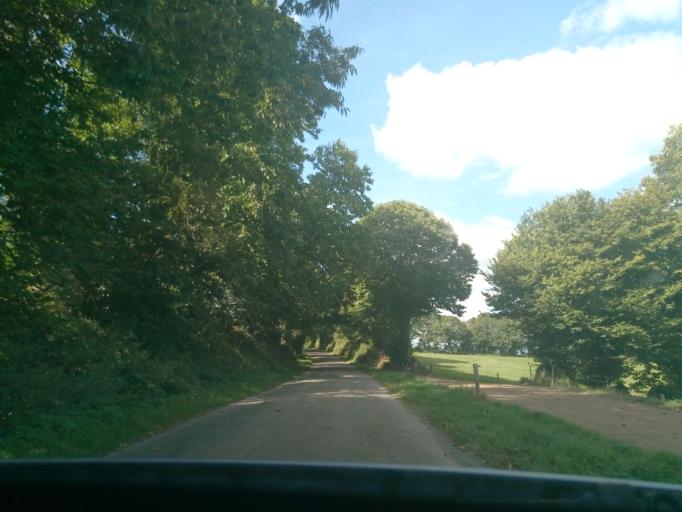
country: FR
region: Brittany
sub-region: Departement du Morbihan
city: Gourin
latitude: 48.1498
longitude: -3.5796
